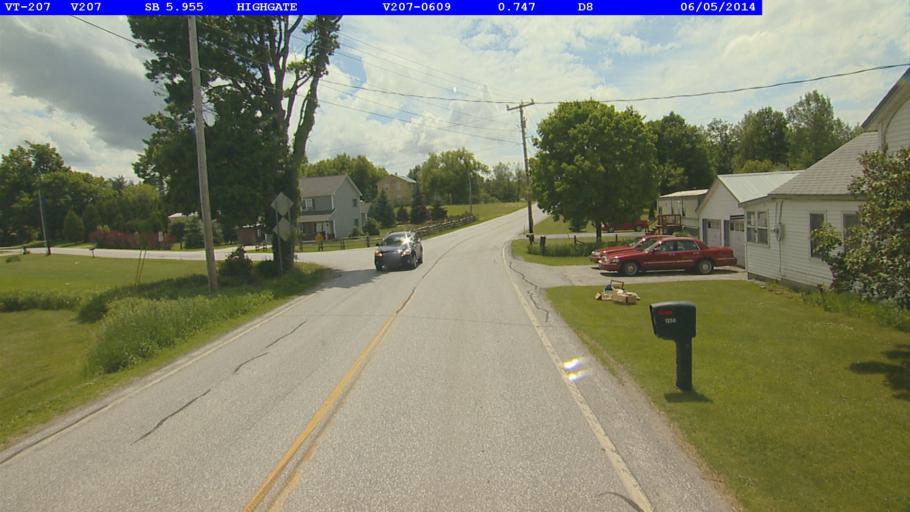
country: US
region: Vermont
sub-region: Franklin County
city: Swanton
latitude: 44.9216
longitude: -73.0531
